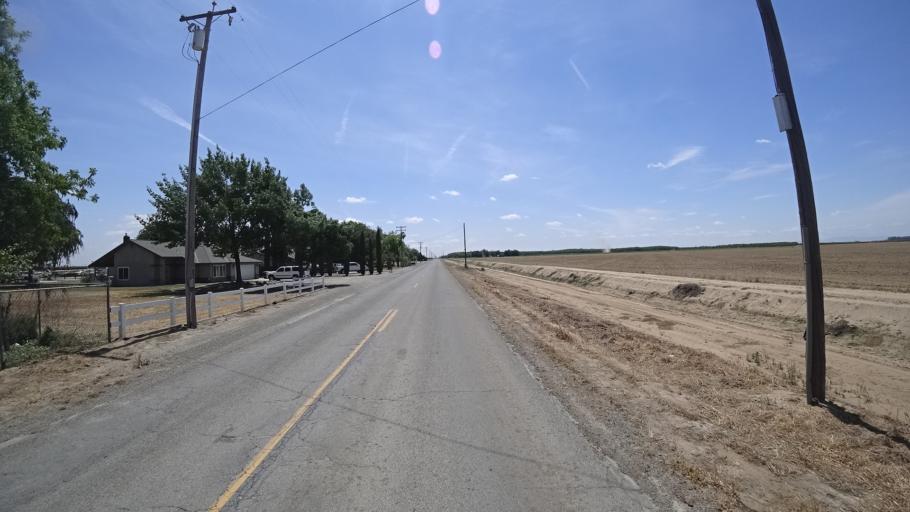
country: US
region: California
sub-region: Kings County
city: Home Garden
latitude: 36.2830
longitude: -119.6728
